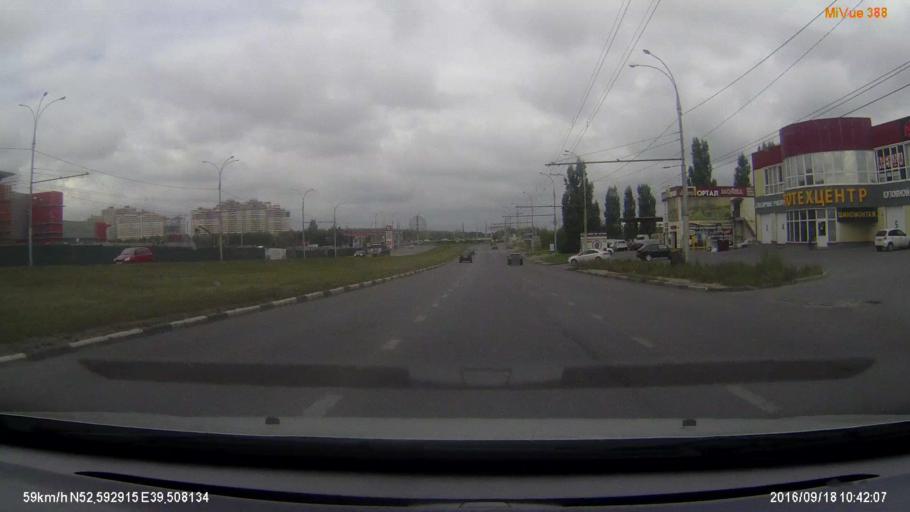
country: RU
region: Lipetsk
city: Syrskoye
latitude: 52.5928
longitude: 39.5083
